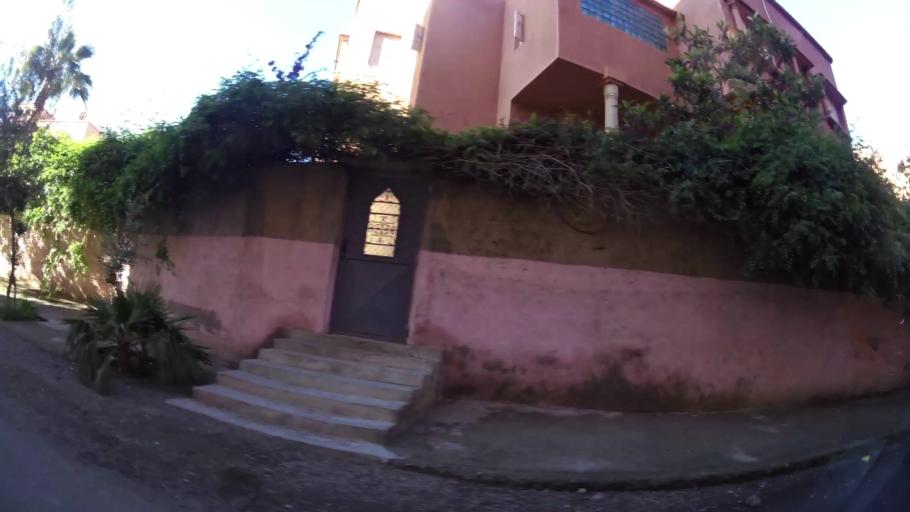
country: MA
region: Marrakech-Tensift-Al Haouz
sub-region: Marrakech
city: Marrakesh
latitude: 31.6512
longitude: -8.0190
